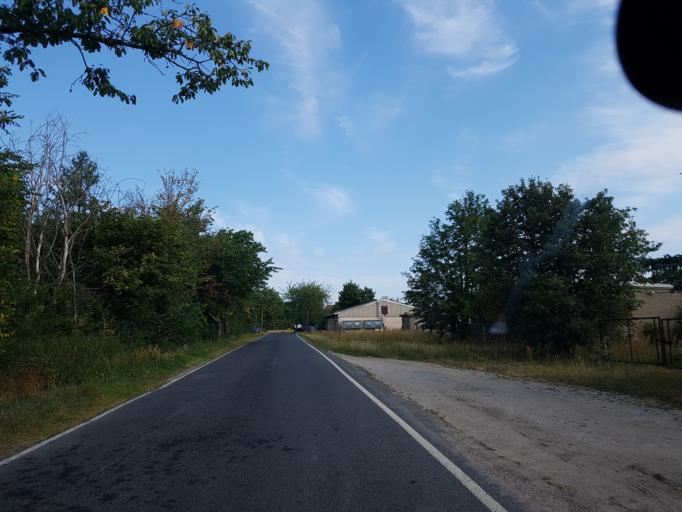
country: DE
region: Brandenburg
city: Drahnsdorf
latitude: 51.8503
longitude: 13.6215
